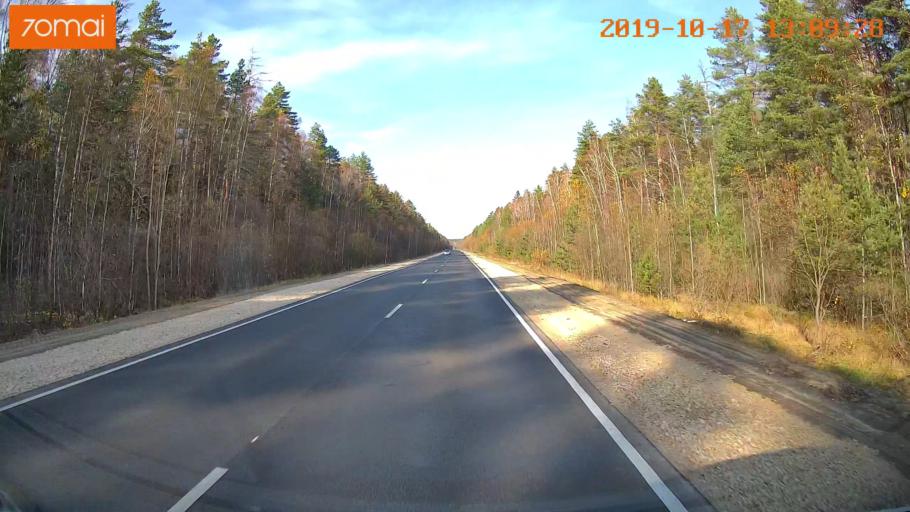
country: RU
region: Rjazan
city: Syntul
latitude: 55.0044
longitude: 41.2628
